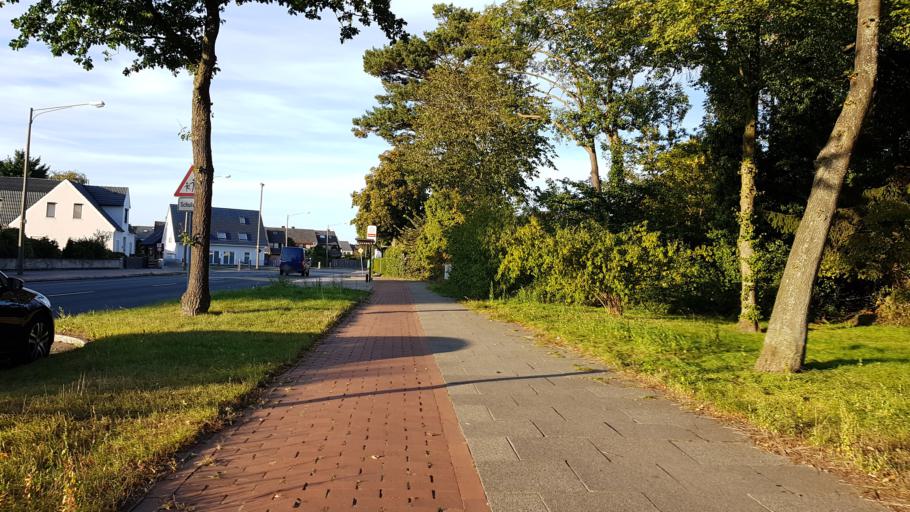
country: DE
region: Lower Saxony
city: Riede
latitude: 53.0417
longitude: 8.9123
